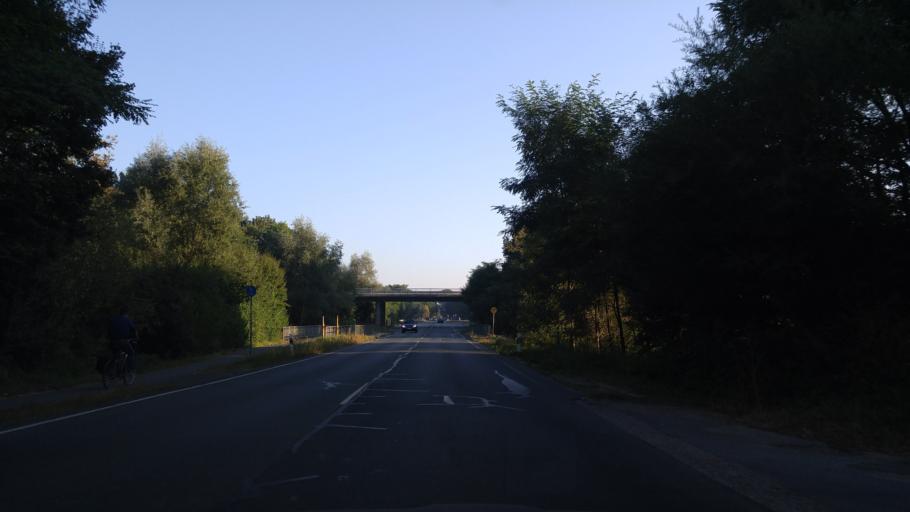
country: DE
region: Bavaria
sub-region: Regierungsbezirk Mittelfranken
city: Erlangen
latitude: 49.5399
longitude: 10.9841
